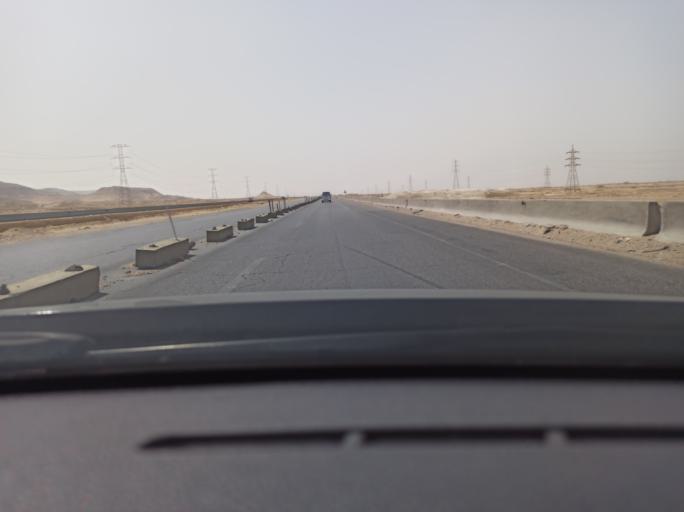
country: EG
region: Muhafazat Bani Suwayf
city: Bush
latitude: 29.1246
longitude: 31.2225
